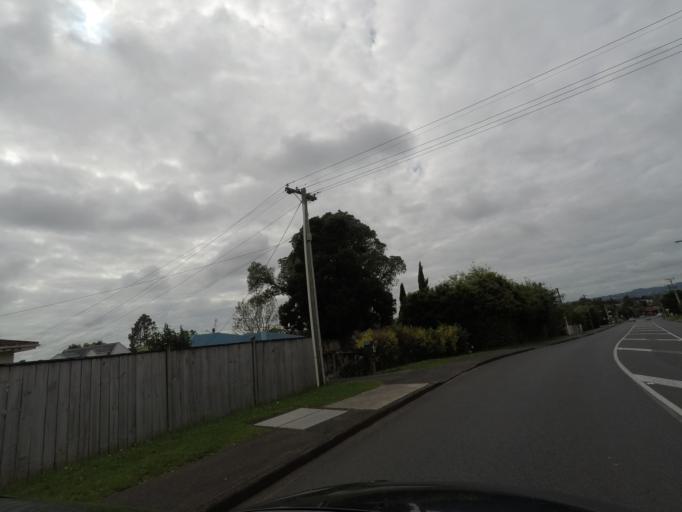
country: NZ
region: Auckland
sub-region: Auckland
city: Rosebank
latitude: -36.8482
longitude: 174.6088
